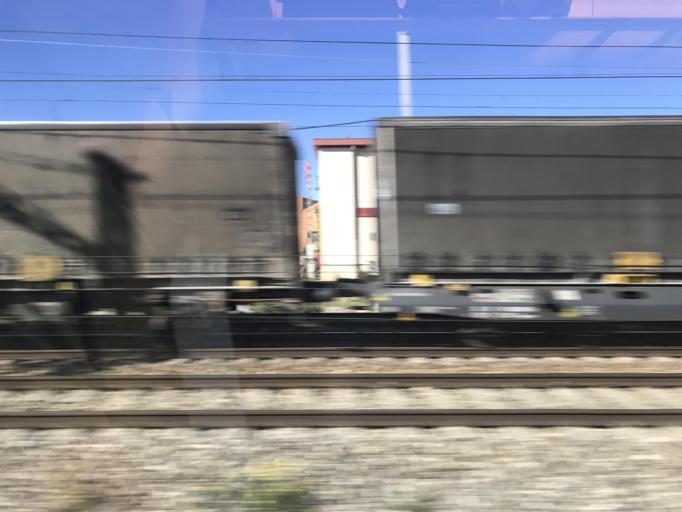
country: ES
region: Madrid
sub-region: Provincia de Madrid
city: Las Tablas
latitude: 40.4994
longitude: -3.6793
